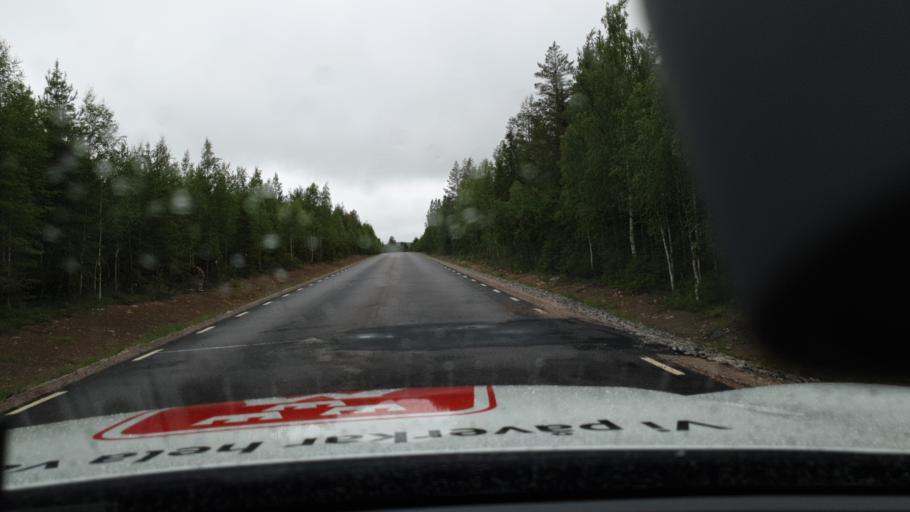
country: SE
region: Norrbotten
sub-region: Overtornea Kommun
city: OEvertornea
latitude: 66.4663
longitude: 23.4685
